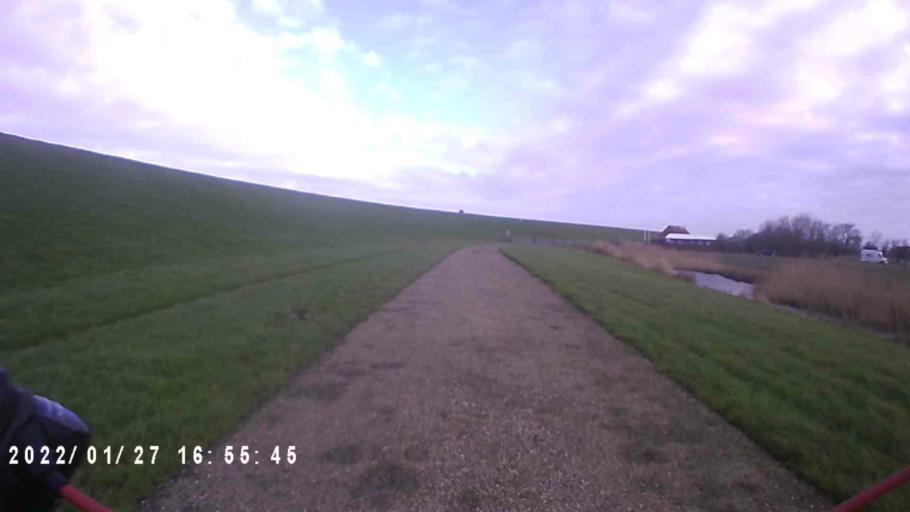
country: NL
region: Friesland
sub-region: Gemeente Dongeradeel
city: Anjum
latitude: 53.4067
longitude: 6.0677
